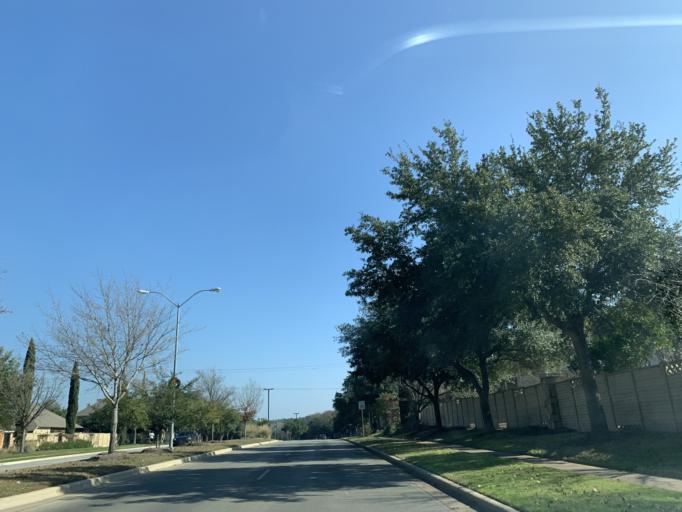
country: US
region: Texas
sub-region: Travis County
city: Windemere
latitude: 30.5073
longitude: -97.6249
